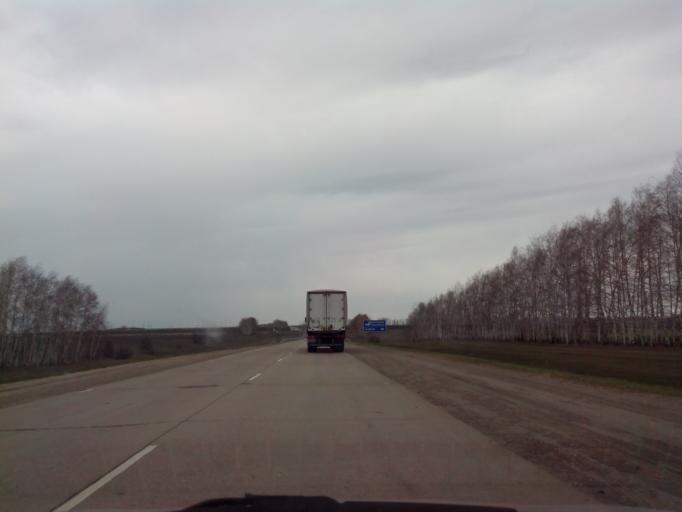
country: RU
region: Tambov
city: Pokrovo-Prigorodnoye
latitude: 52.6536
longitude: 41.3404
